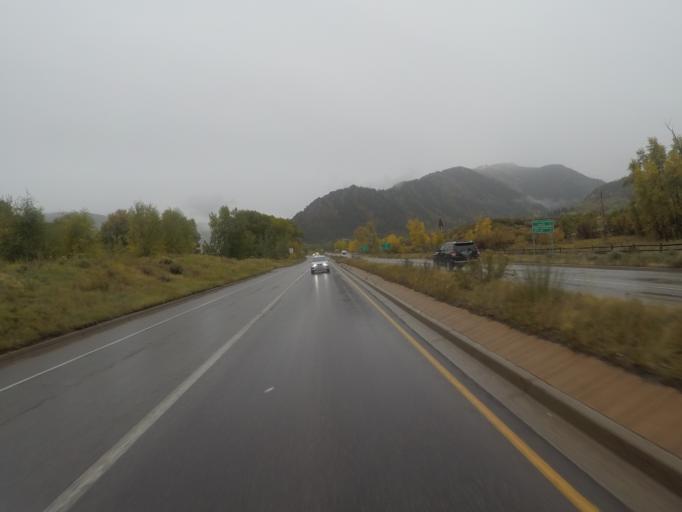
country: US
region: Colorado
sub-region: Pitkin County
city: Aspen
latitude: 39.1984
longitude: -106.8442
